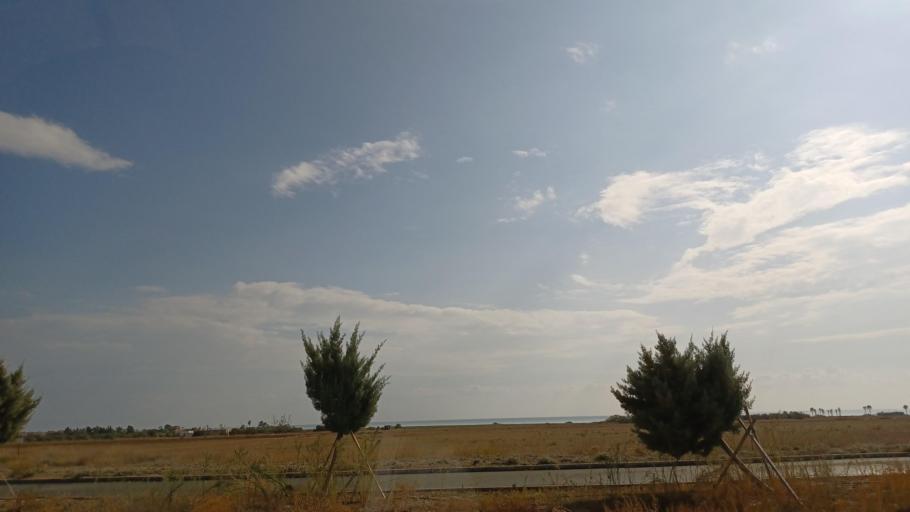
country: CY
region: Larnaka
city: Tersefanou
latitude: 34.8243
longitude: 33.5459
